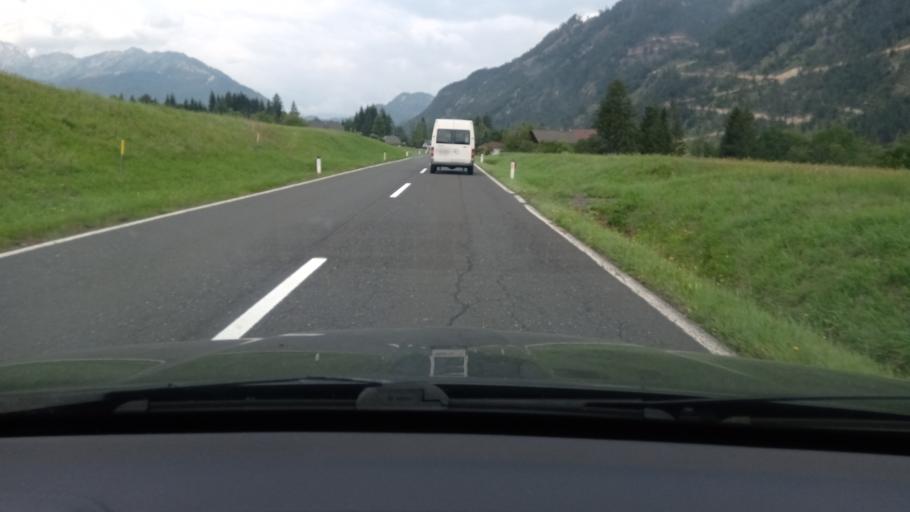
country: AT
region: Carinthia
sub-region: Politischer Bezirk Hermagor
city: Hermagor
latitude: 46.6641
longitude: 13.3068
